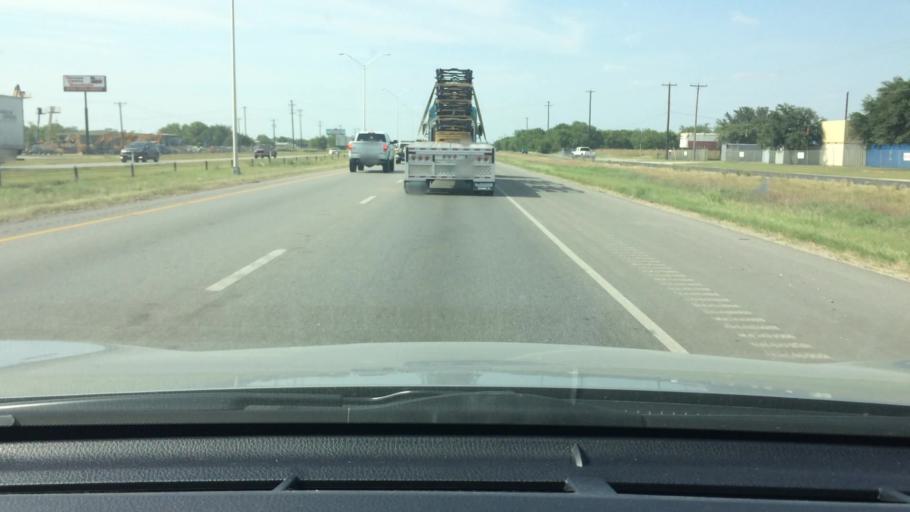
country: US
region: Texas
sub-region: Bexar County
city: China Grove
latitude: 29.4136
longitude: -98.3895
